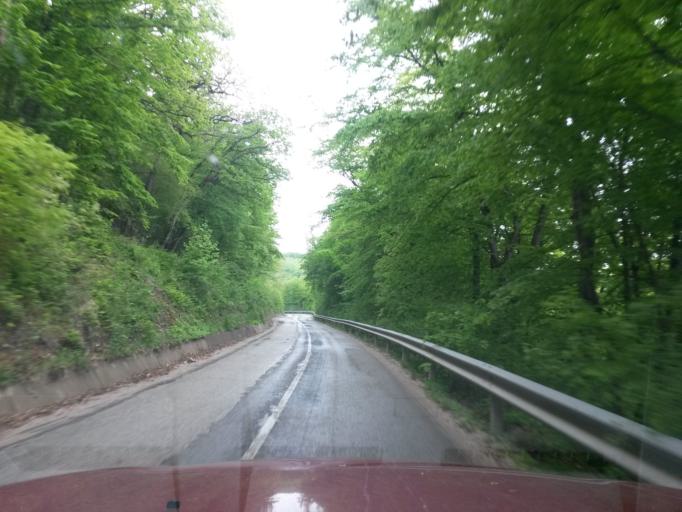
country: SK
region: Kosicky
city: Roznava
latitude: 48.5657
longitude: 20.4728
